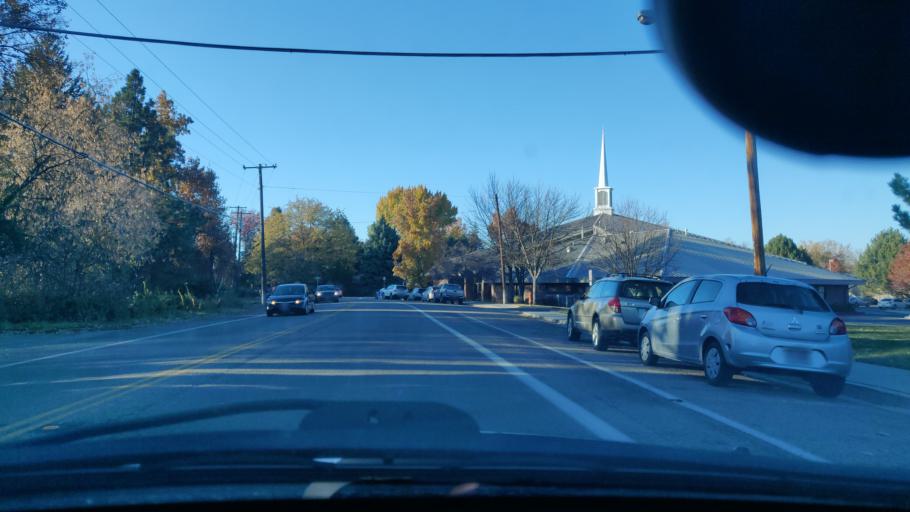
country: US
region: Idaho
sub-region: Ada County
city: Boise
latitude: 43.6000
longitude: -116.2071
